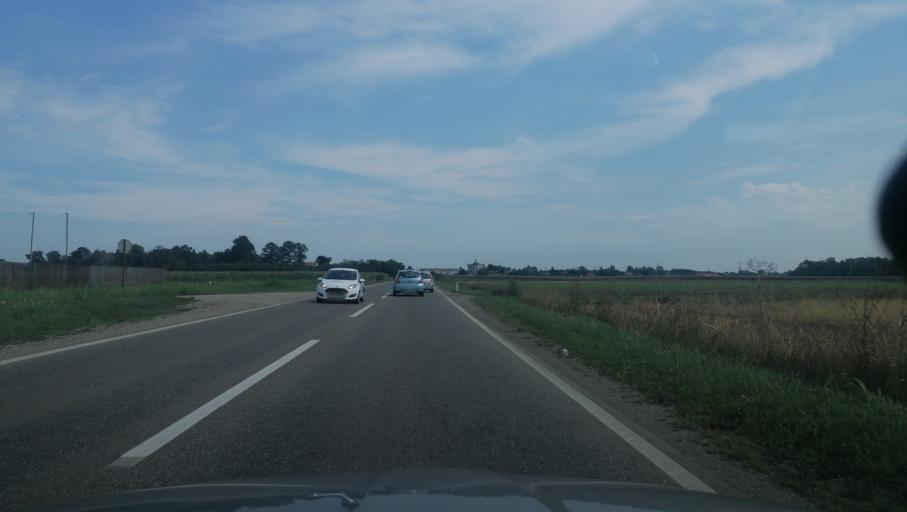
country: BA
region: Republika Srpska
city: Dvorovi
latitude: 44.7872
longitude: 19.2611
